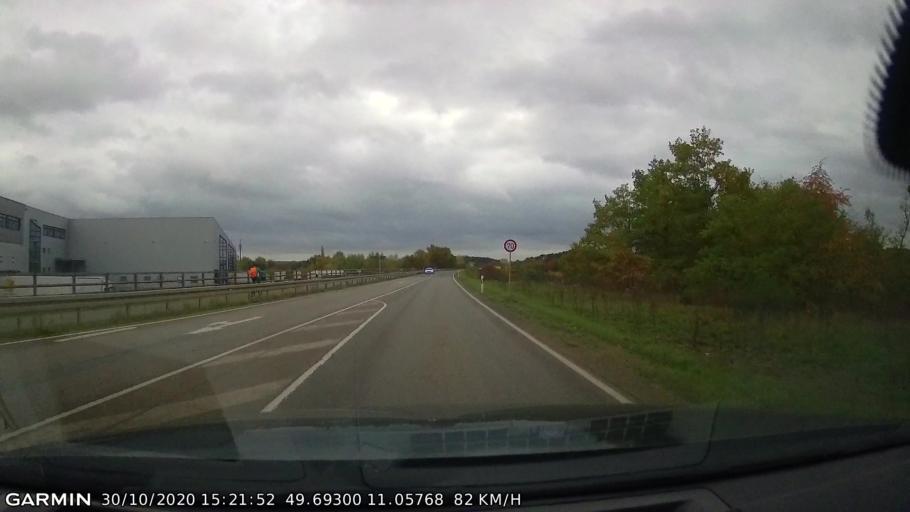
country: DE
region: Bavaria
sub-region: Upper Franconia
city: Forchheim
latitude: 49.6931
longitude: 11.0579
